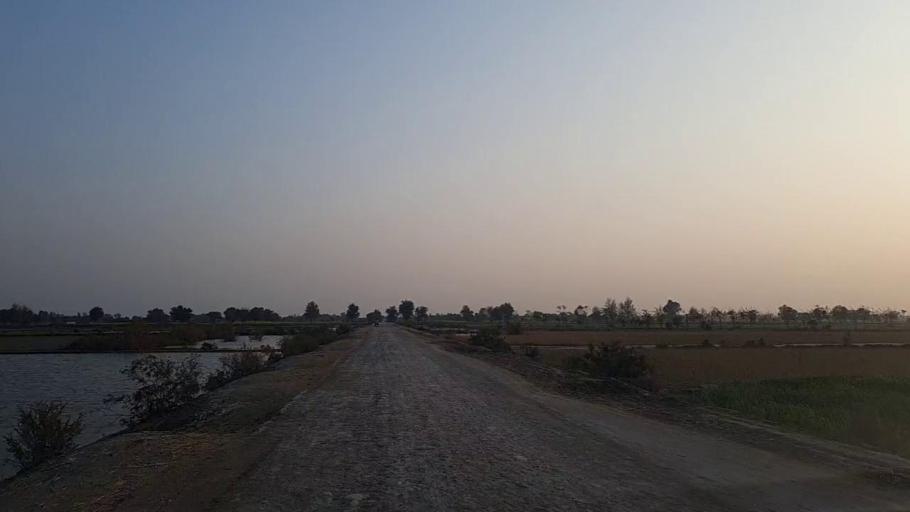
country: PK
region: Sindh
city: Daur
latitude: 26.4219
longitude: 68.3678
